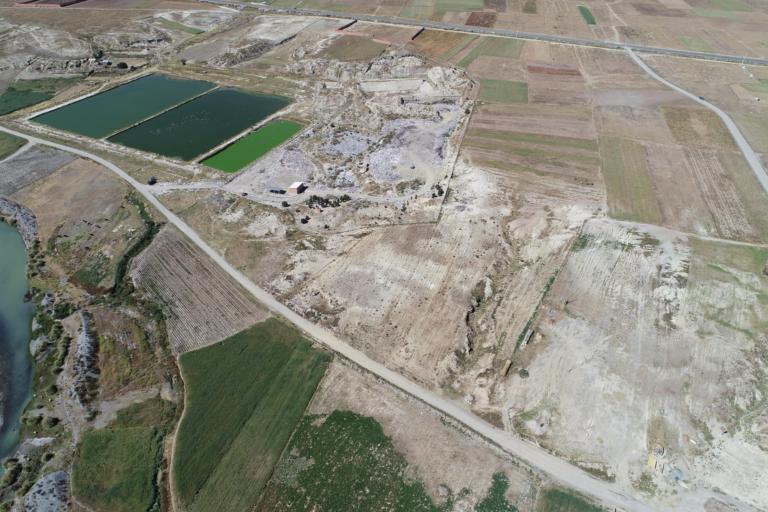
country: BO
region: La Paz
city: Achacachi
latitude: -16.0405
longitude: -68.7009
